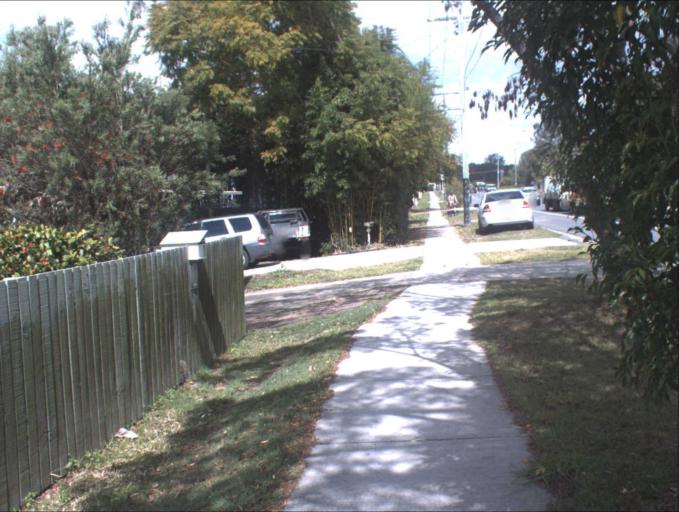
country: AU
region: Queensland
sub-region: Logan
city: Park Ridge South
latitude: -27.6922
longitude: 153.0105
